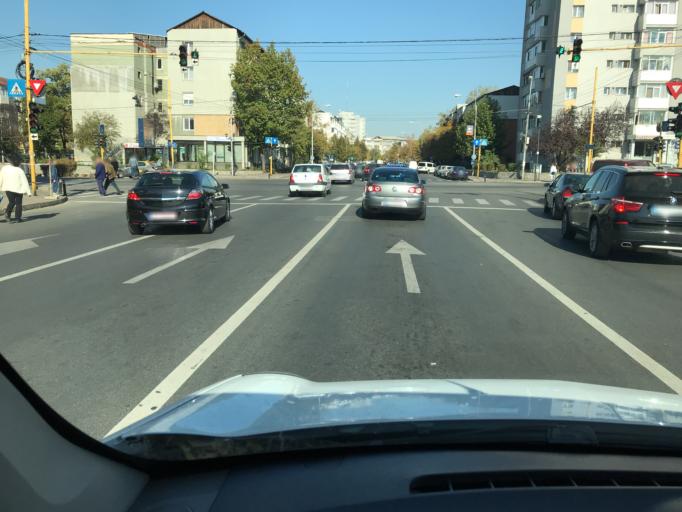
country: RO
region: Olt
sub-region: Municipiul Slatina
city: Slatina
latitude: 44.4323
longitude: 24.3729
